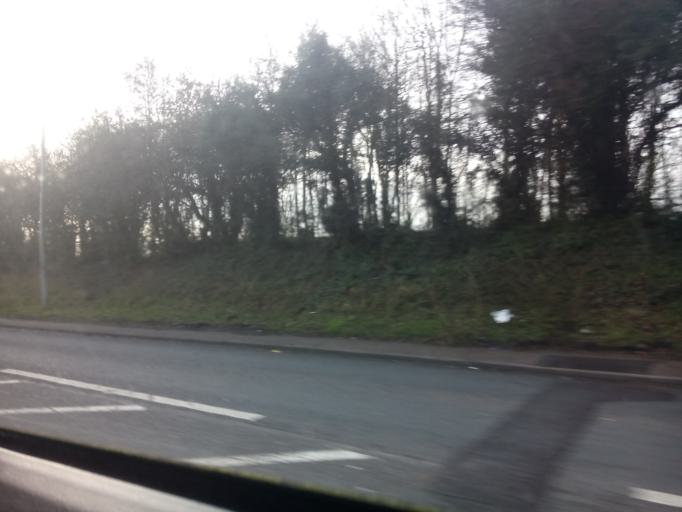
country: GB
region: England
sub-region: Worcestershire
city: Bromsgrove
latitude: 52.3687
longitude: -2.0462
